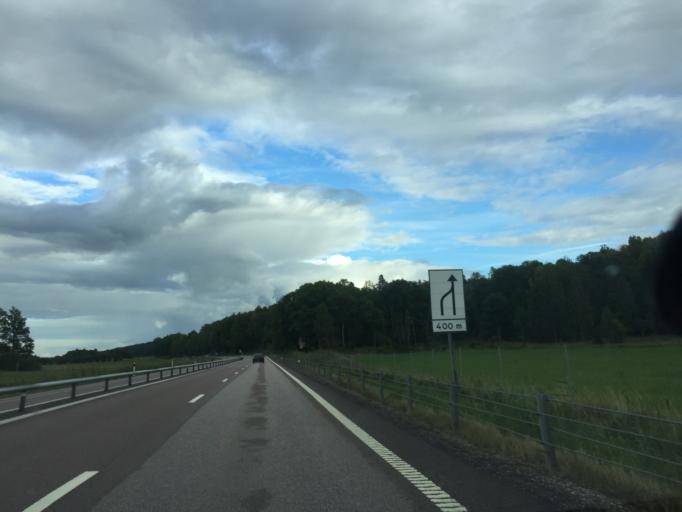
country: SE
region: Vaestmanland
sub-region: Arboga Kommun
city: Tyringe
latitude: 59.4046
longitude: 15.9700
